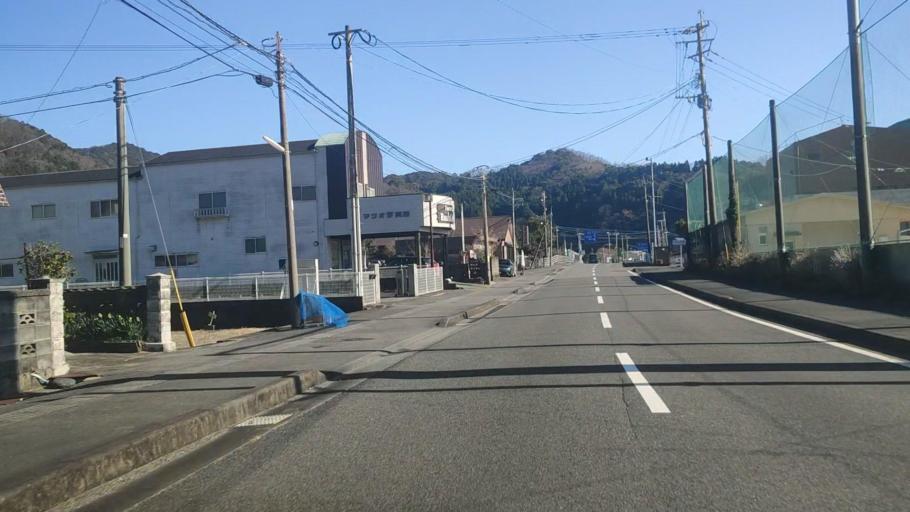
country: JP
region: Oita
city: Saiki
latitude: 32.8014
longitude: 131.9207
